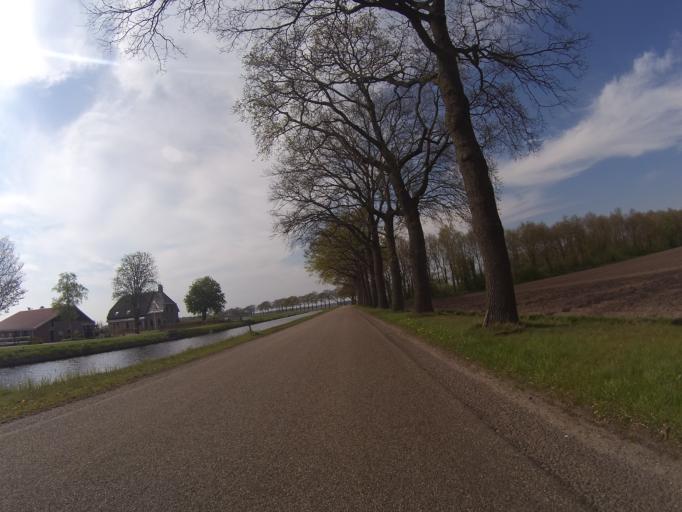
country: NL
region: Drenthe
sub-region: Gemeente Coevorden
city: Sleen
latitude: 52.7372
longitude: 6.7869
